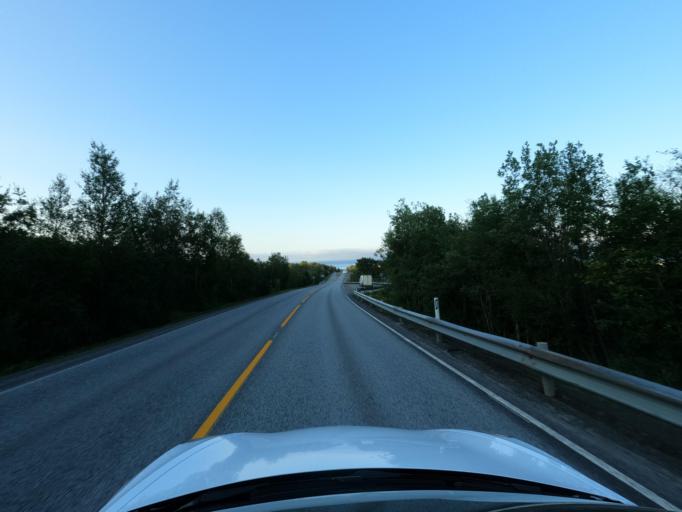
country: NO
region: Troms
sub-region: Harstad
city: Harstad
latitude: 68.7393
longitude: 16.5582
